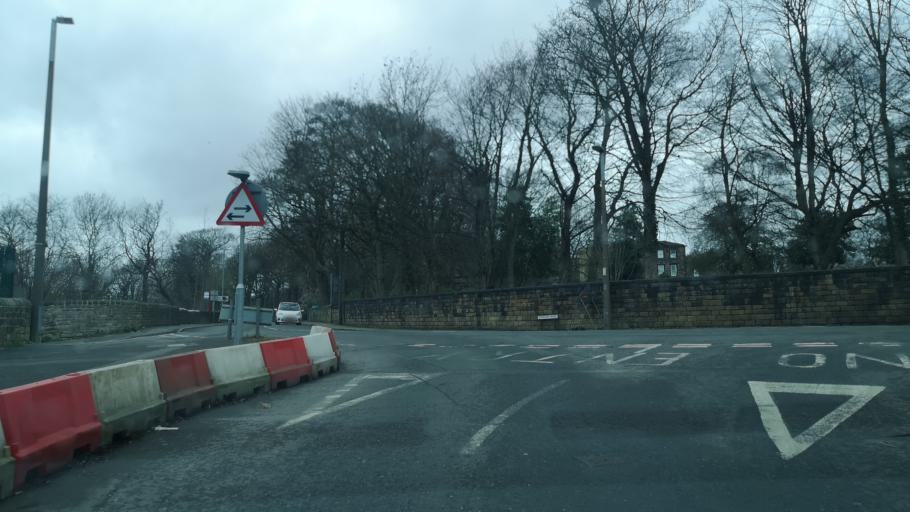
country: GB
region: England
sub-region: Kirklees
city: Dewsbury
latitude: 53.6865
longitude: -1.6474
